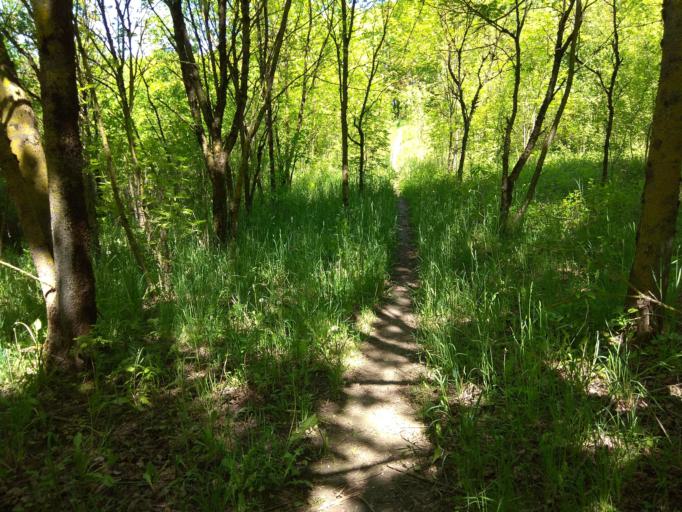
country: BY
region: Grodnenskaya
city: Hrodna
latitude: 53.7127
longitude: 23.7990
